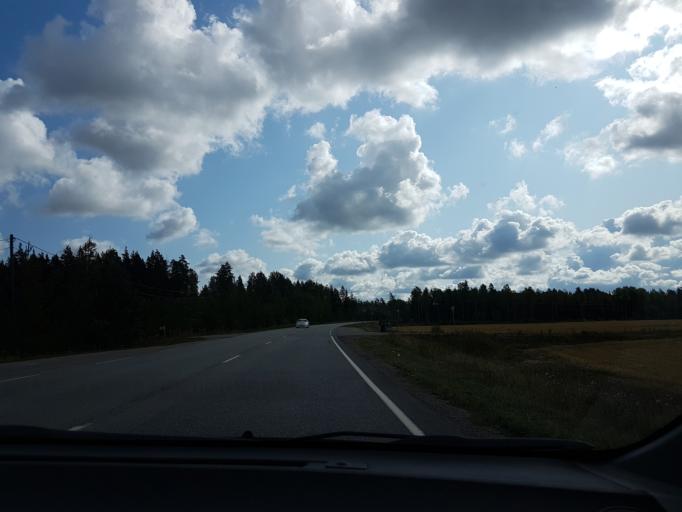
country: FI
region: Uusimaa
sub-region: Helsinki
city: Nickby
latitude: 60.4702
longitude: 25.2610
